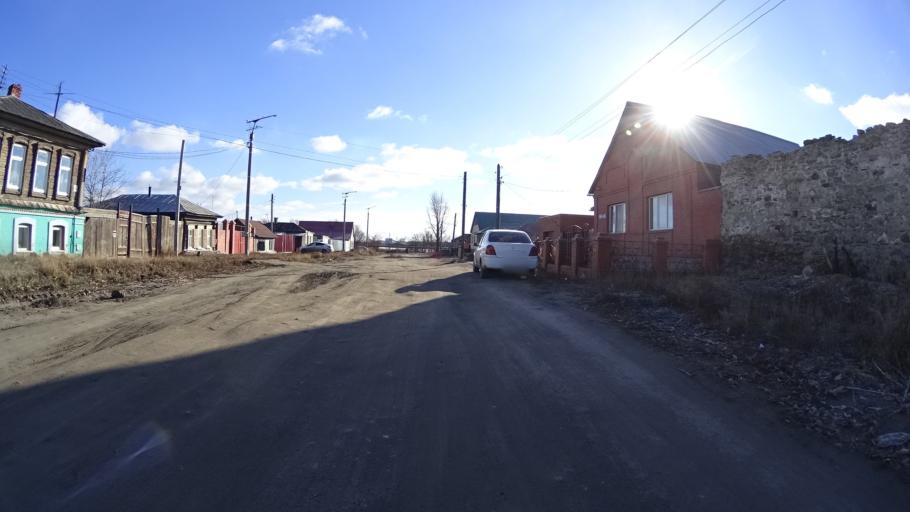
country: RU
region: Chelyabinsk
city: Troitsk
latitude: 54.0831
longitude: 61.5686
